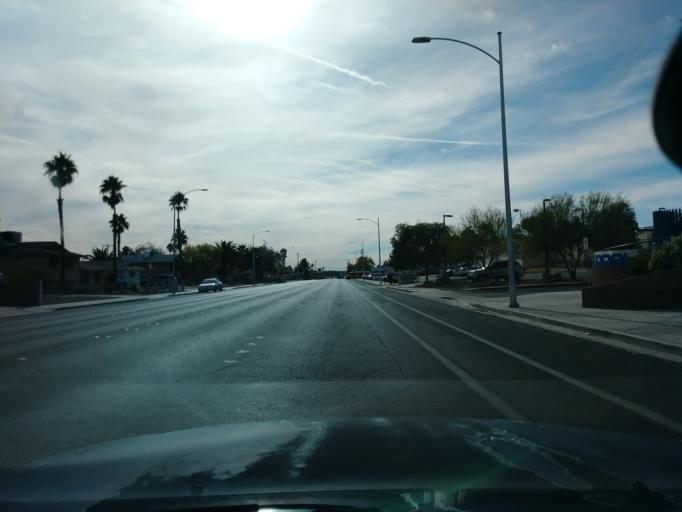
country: US
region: Nevada
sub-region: Clark County
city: Spring Valley
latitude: 36.1704
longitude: -115.2332
